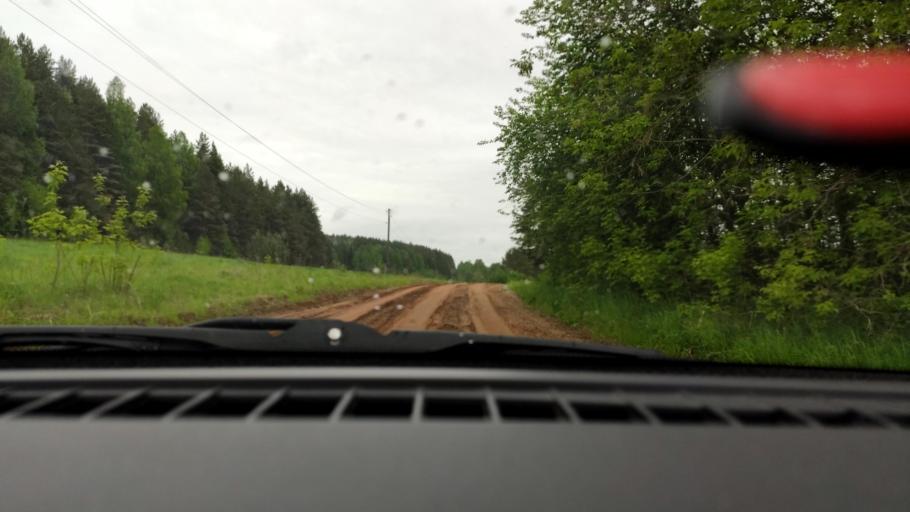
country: RU
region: Perm
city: Karagay
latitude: 58.2533
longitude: 54.8760
